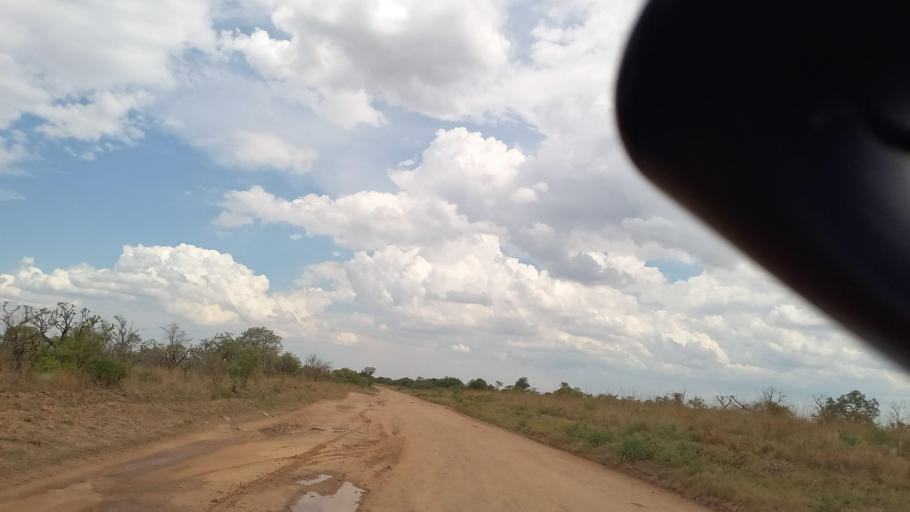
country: ZM
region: Southern
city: Nakambala
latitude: -16.0547
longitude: 27.9871
